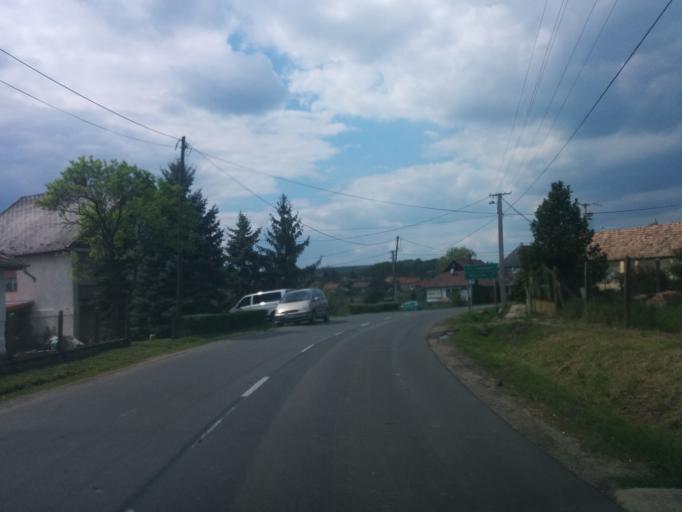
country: HU
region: Nograd
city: Palotas
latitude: 47.8225
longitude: 19.5890
